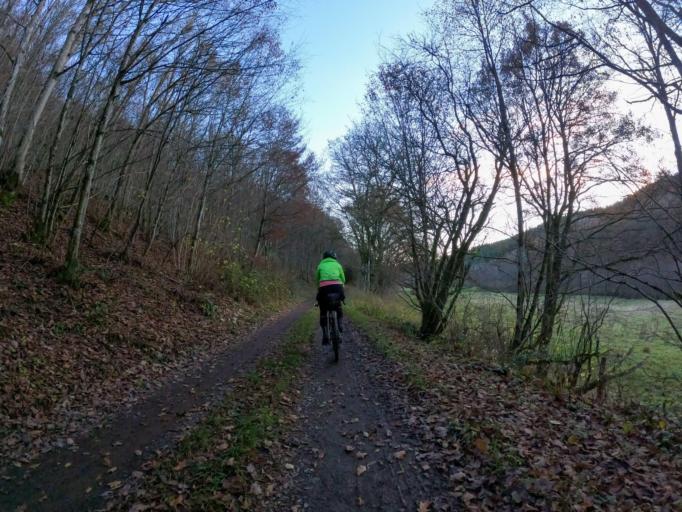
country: LU
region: Diekirch
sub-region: Canton de Wiltz
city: Bavigne
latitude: 49.9317
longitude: 5.8445
